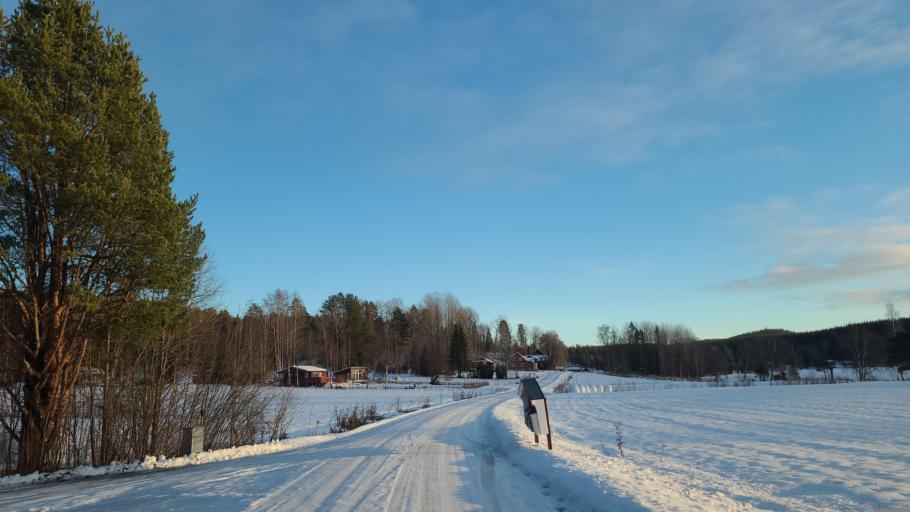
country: SE
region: Gaevleborg
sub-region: Bollnas Kommun
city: Kilafors
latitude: 61.3966
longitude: 16.6753
